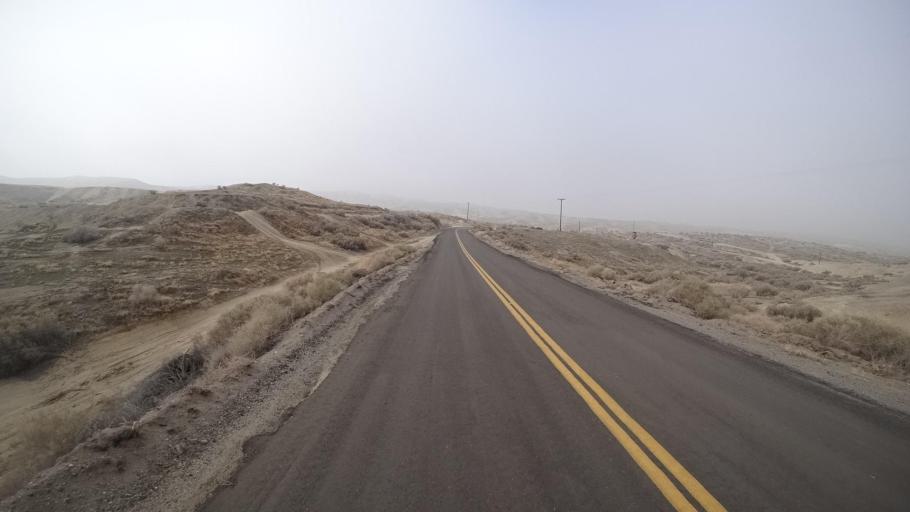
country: US
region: California
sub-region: Kern County
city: Ford City
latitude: 35.1649
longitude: -119.3903
